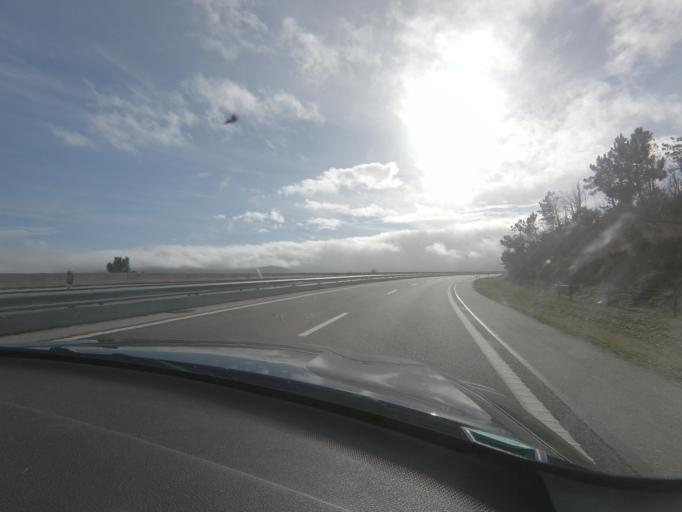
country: PT
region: Viseu
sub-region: Lamego
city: Lamego
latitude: 41.0507
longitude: -7.8410
